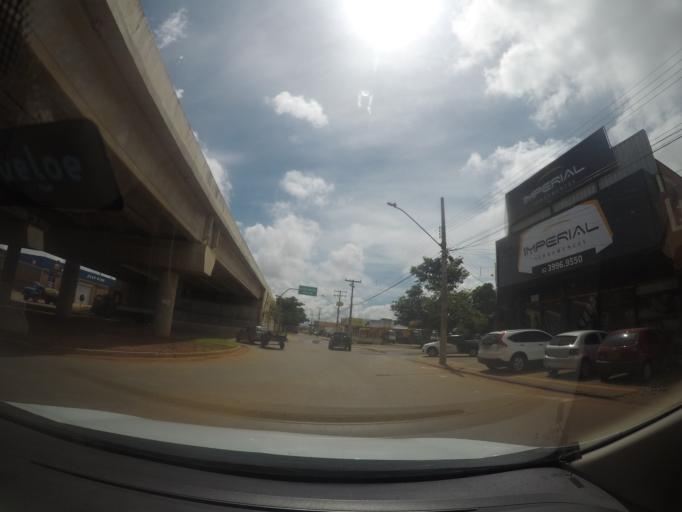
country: BR
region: Goias
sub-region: Goiania
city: Goiania
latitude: -16.7005
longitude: -49.3337
